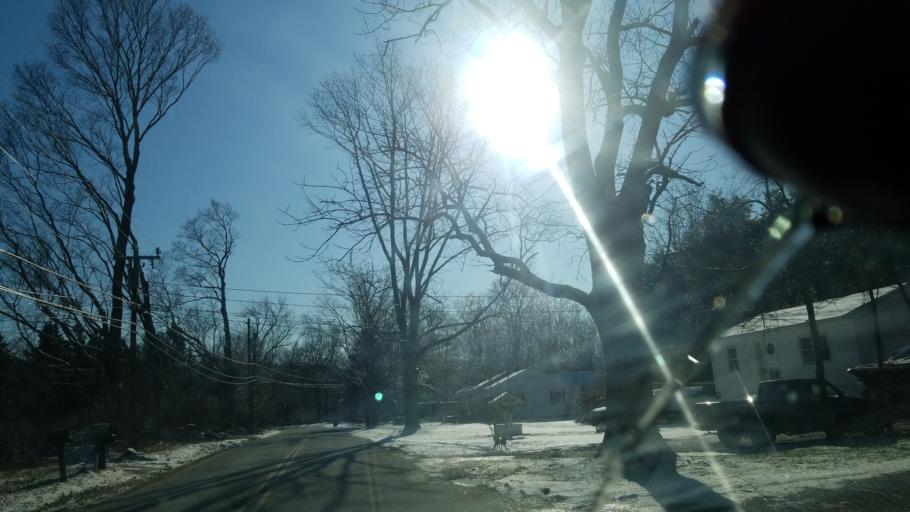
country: US
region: Connecticut
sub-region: Windham County
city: Danielson
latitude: 41.7914
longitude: -71.8800
